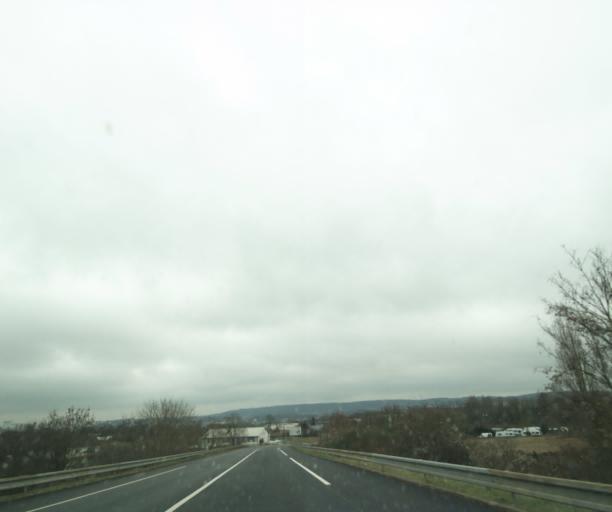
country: FR
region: Ile-de-France
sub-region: Departement de l'Essonne
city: Champlan
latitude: 48.7124
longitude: 2.2808
